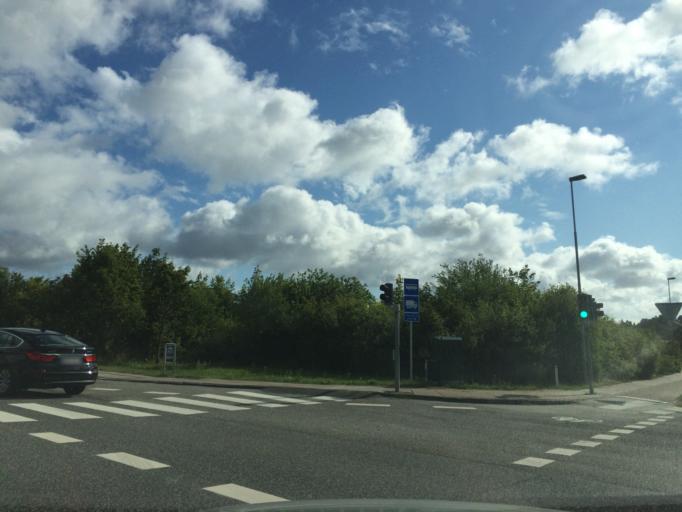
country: DK
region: Central Jutland
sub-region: Arhus Kommune
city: Beder
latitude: 56.1076
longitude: 10.2075
